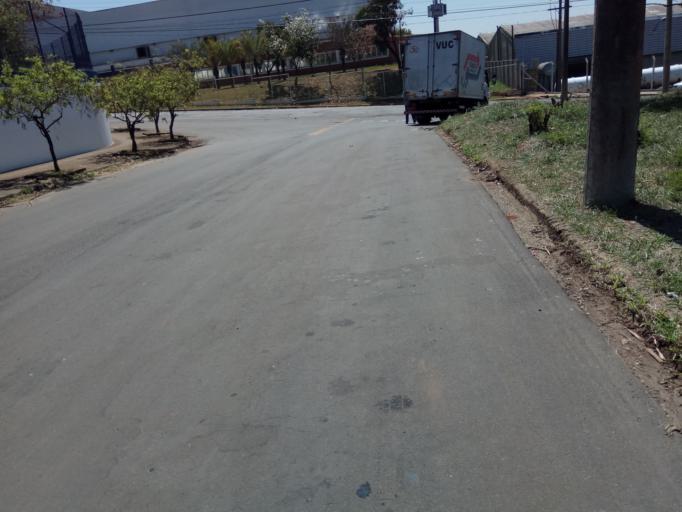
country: BR
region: Sao Paulo
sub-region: Piracicaba
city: Piracicaba
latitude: -22.7309
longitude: -47.5946
